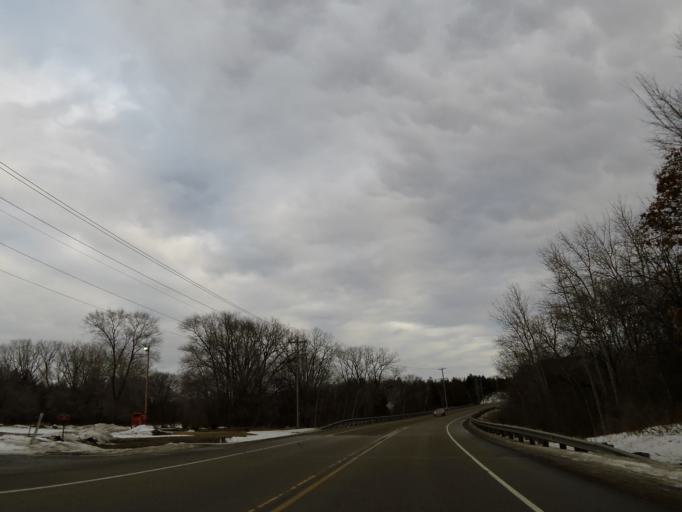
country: US
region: Minnesota
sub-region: Washington County
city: Bayport
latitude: 45.0422
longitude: -92.7582
